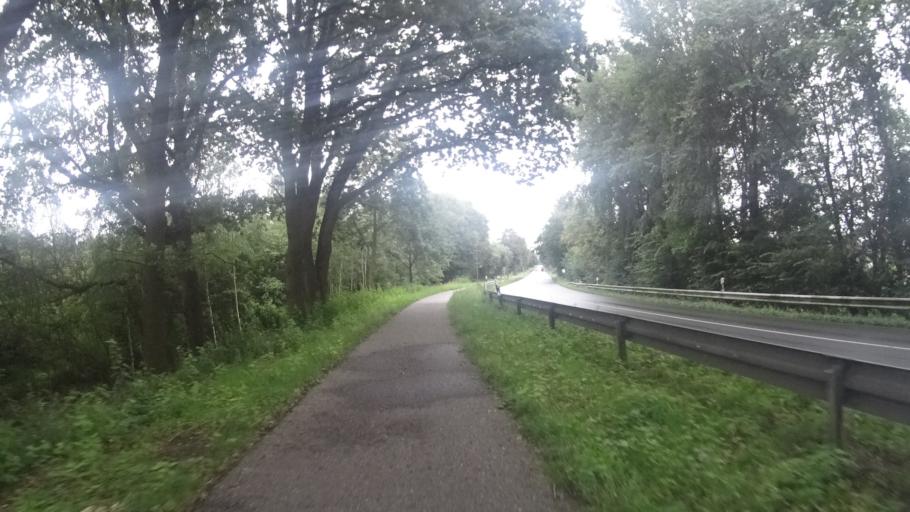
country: DE
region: Schleswig-Holstein
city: Elmshorn
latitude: 53.7740
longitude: 9.6704
